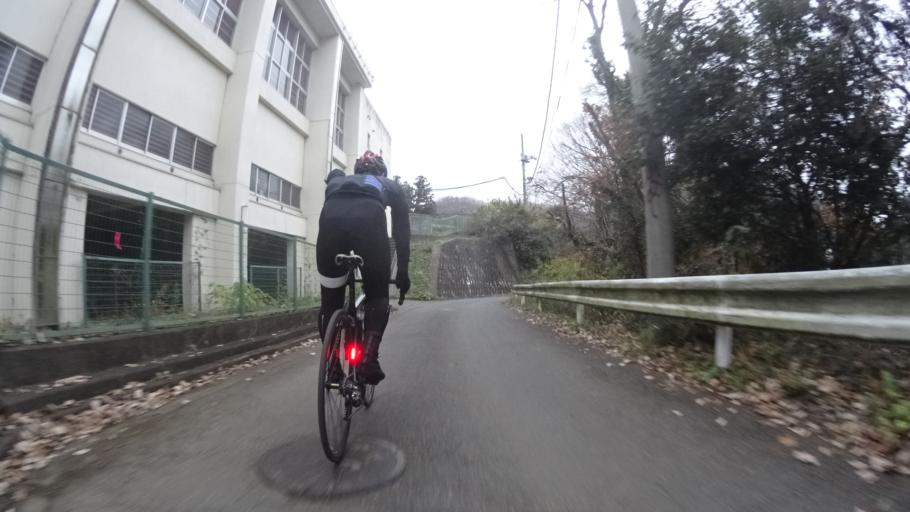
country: JP
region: Yamanashi
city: Uenohara
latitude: 35.6158
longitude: 139.1655
